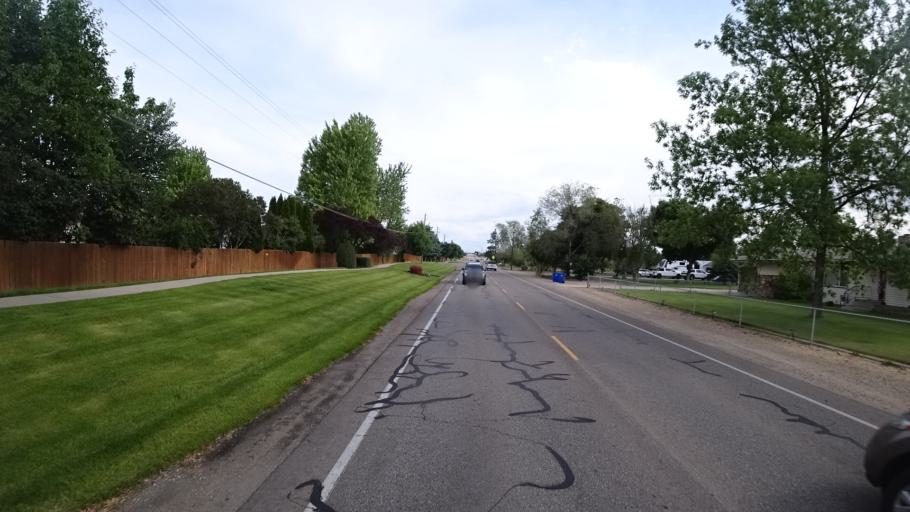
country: US
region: Idaho
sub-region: Ada County
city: Meridian
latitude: 43.5843
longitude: -116.3746
